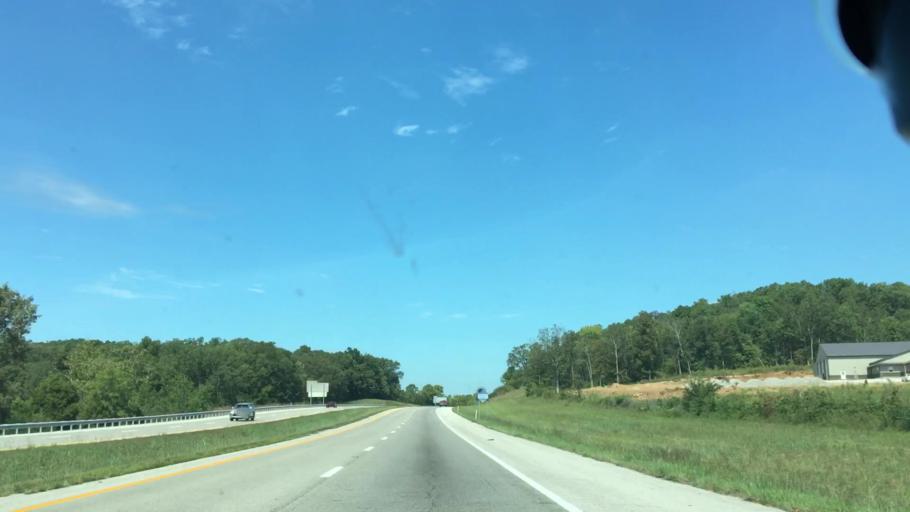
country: US
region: Kentucky
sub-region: Christian County
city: Hopkinsville
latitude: 36.9037
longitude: -87.4717
